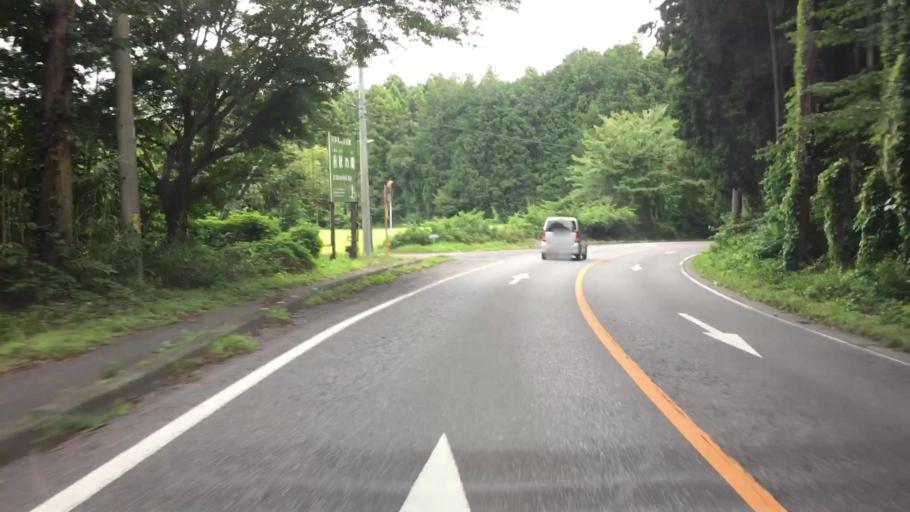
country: JP
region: Tochigi
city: Imaichi
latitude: 36.7145
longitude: 139.7521
